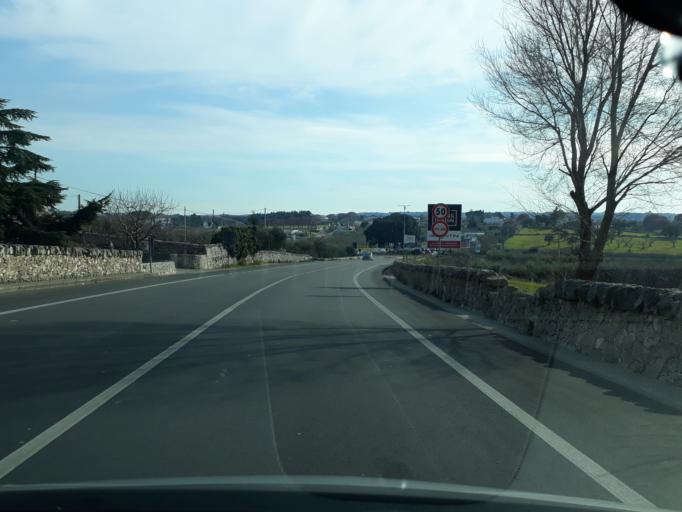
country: IT
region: Apulia
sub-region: Provincia di Bari
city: Locorotondo
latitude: 40.7507
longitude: 17.3286
